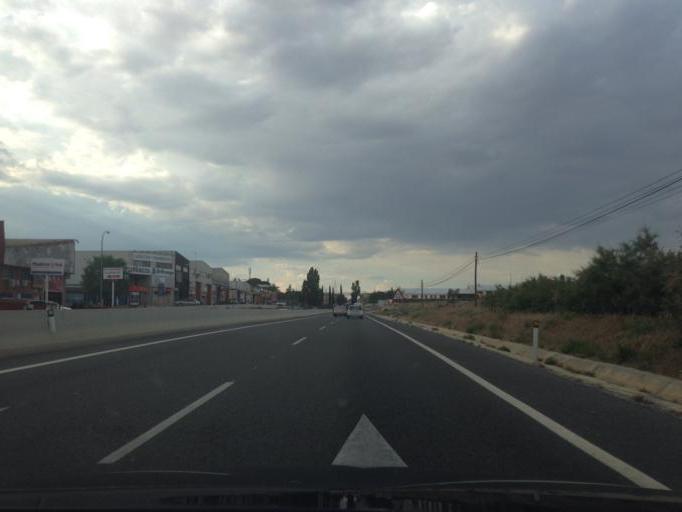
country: ES
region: Madrid
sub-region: Provincia de Madrid
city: Ajalvir
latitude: 40.5007
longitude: -3.4793
